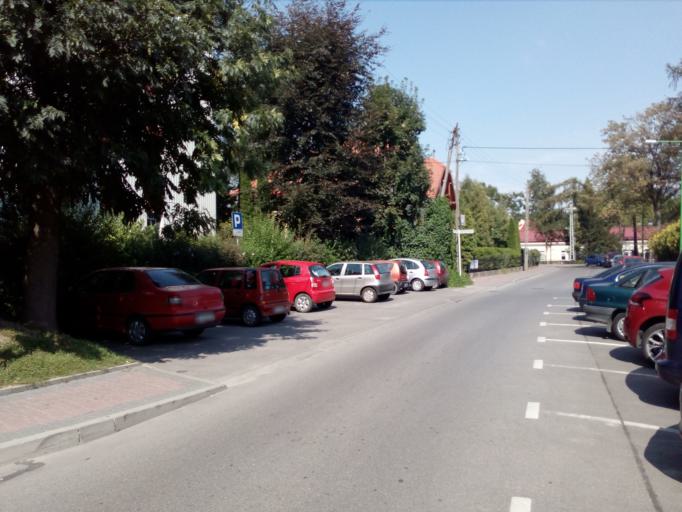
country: PL
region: Subcarpathian Voivodeship
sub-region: Powiat lancucki
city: Lancut
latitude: 50.0653
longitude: 22.2317
